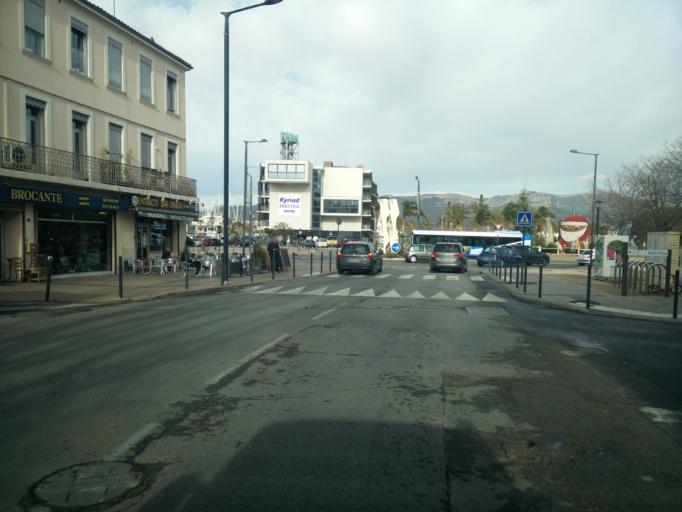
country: FR
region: Provence-Alpes-Cote d'Azur
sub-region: Departement du Var
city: La Seyne-sur-Mer
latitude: 43.1007
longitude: 5.8840
